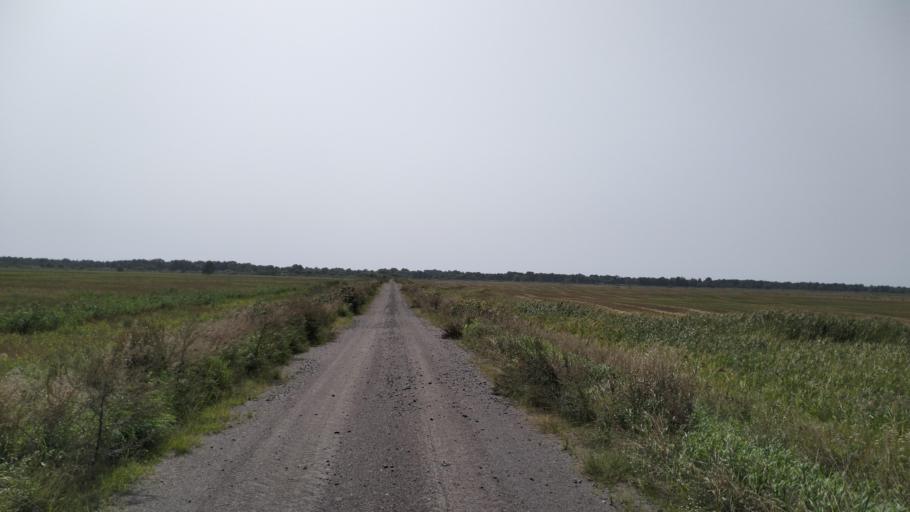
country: BY
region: Brest
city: Davyd-Haradok
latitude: 51.9769
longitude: 27.1745
